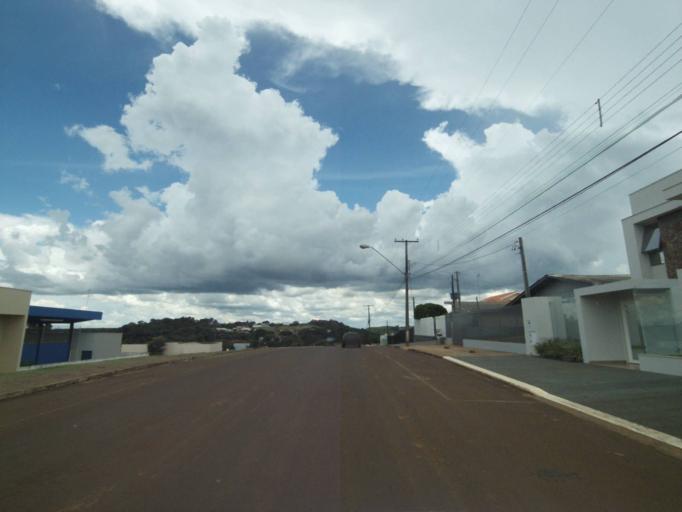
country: BR
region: Parana
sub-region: Guaraniacu
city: Guaraniacu
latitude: -25.1034
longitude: -52.8633
